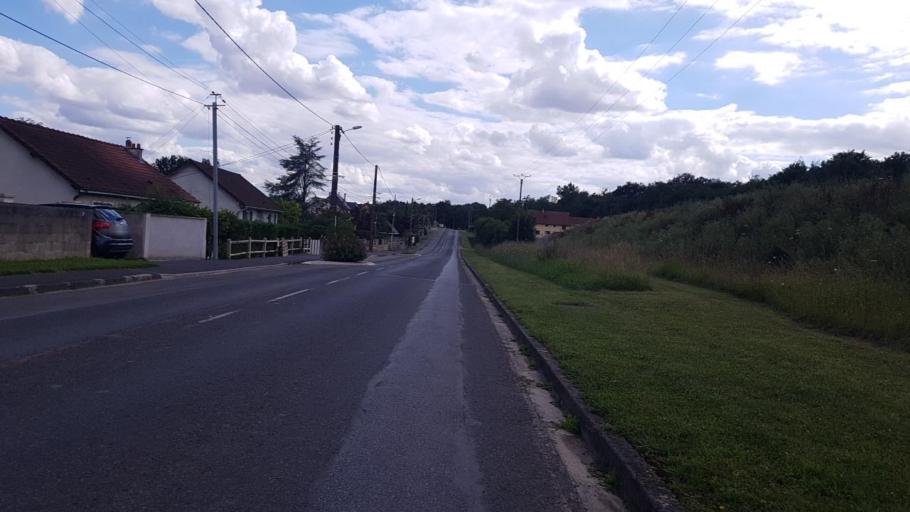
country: FR
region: Picardie
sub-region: Departement de l'Aisne
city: Crezancy
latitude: 49.0828
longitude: 3.5285
